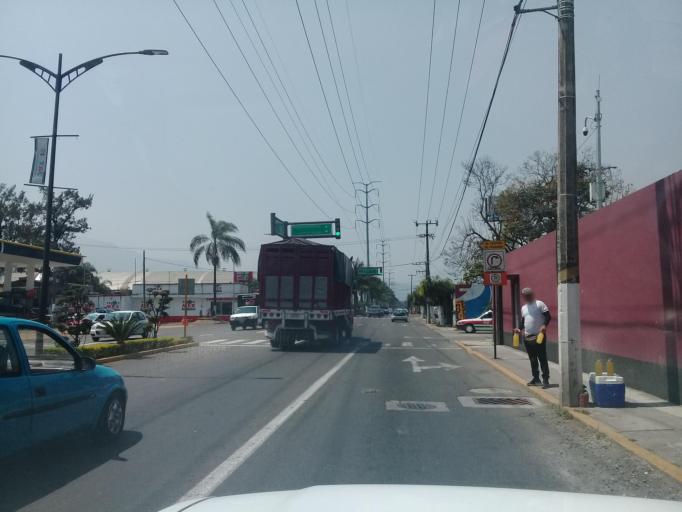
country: MX
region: Veracruz
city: Ixtac Zoquitlan
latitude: 18.8608
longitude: -97.0611
